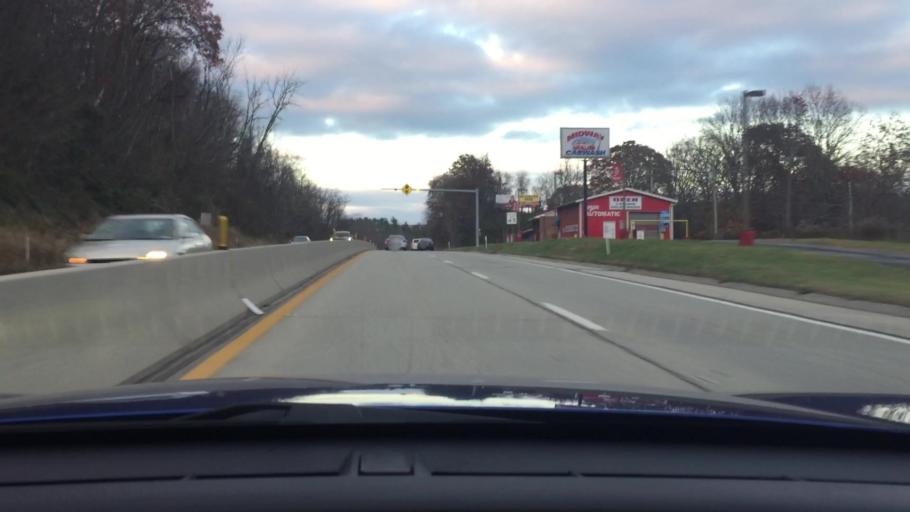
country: US
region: Pennsylvania
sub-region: Westmoreland County
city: Youngwood
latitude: 40.2606
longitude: -79.5675
